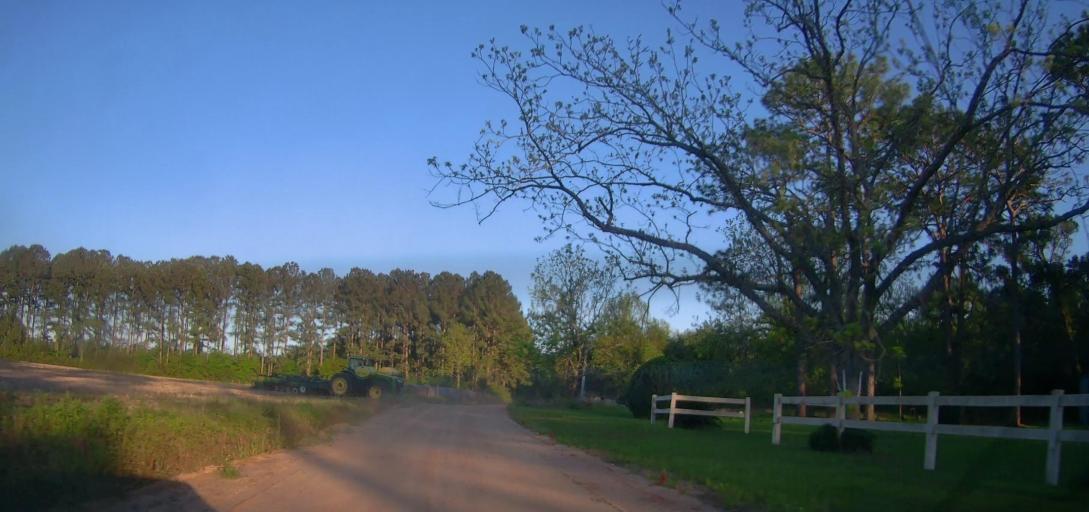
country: US
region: Georgia
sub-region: Irwin County
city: Ocilla
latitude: 31.6504
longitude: -83.2288
